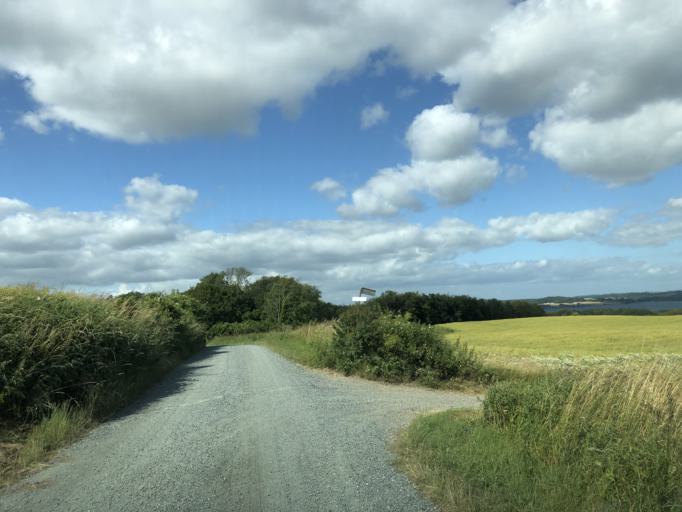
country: DK
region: South Denmark
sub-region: Vejle Kommune
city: Brejning
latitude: 55.6728
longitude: 9.6572
